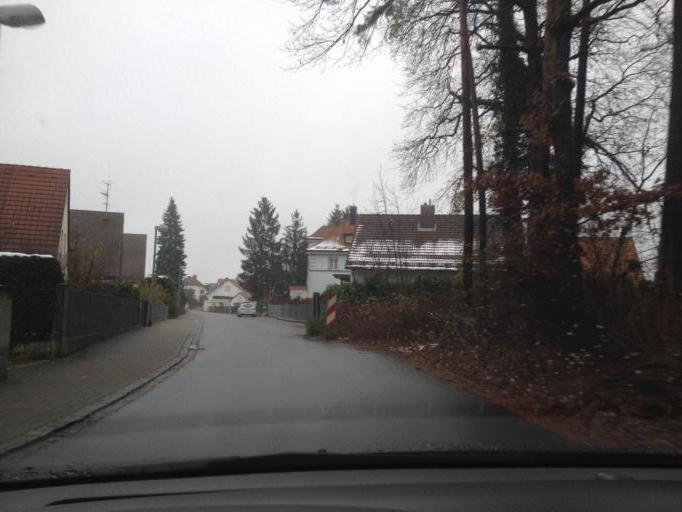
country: DE
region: Bavaria
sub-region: Regierungsbezirk Mittelfranken
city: Lauf an der Pegnitz
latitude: 49.5292
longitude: 11.2716
